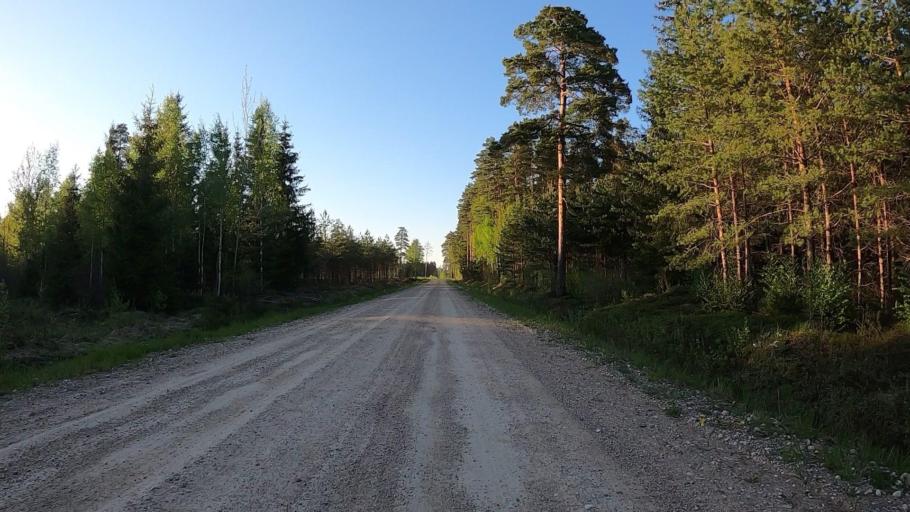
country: LV
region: Kekava
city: Kekava
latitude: 56.7662
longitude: 24.2227
